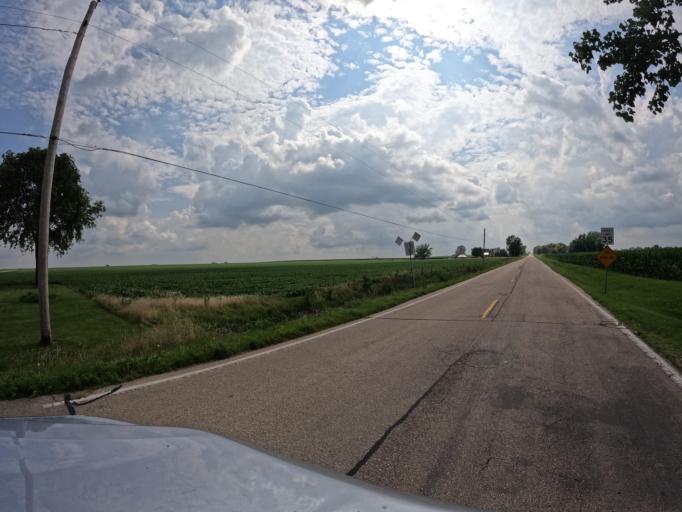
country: US
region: Iowa
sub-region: Clinton County
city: Camanche
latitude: 41.8012
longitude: -90.3601
